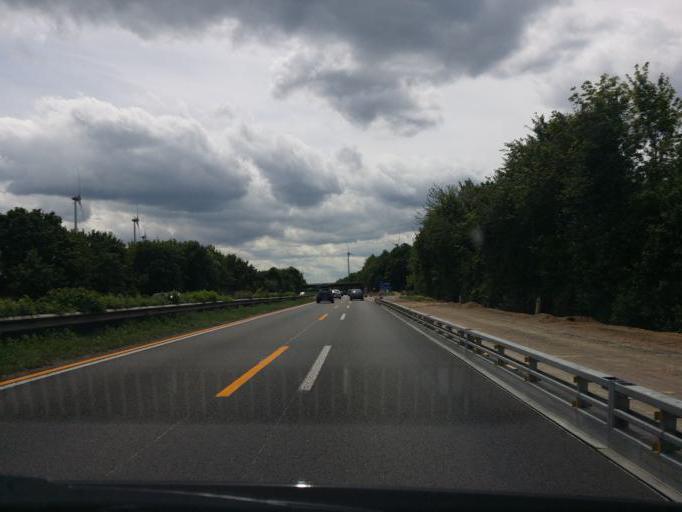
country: DE
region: Rheinland-Pfalz
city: Ober-Saulheim
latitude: 49.8447
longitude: 8.1456
